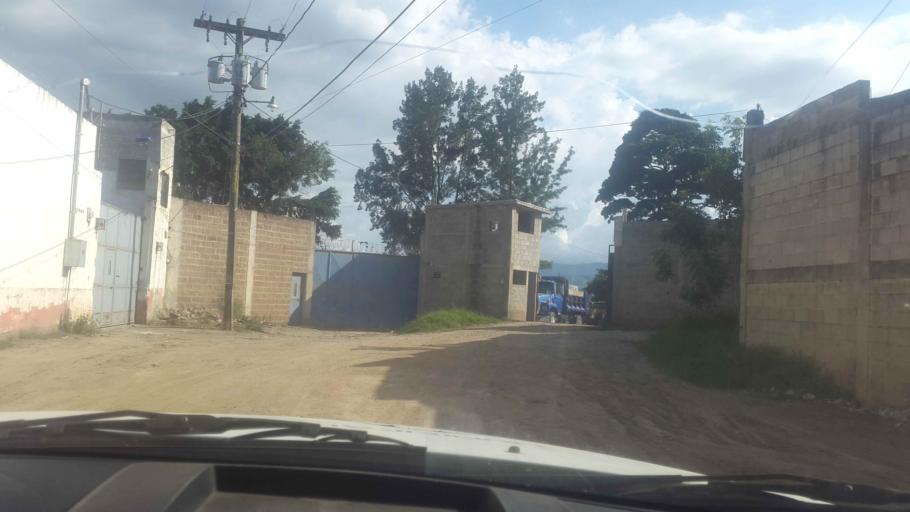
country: GT
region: Guatemala
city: Petapa
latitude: 14.5088
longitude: -90.5421
